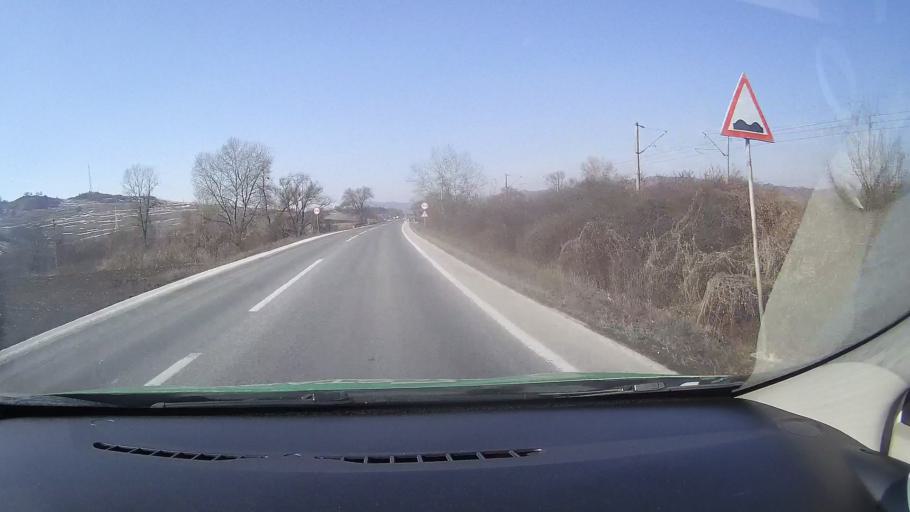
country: RO
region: Mures
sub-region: Comuna Vanatori
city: Vanatori
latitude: 46.2349
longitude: 24.9693
